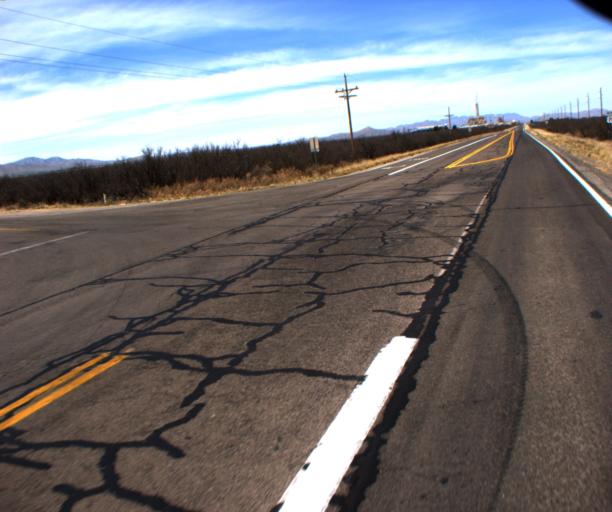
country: US
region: Arizona
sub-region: Cochise County
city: Willcox
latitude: 32.0359
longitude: -109.8789
